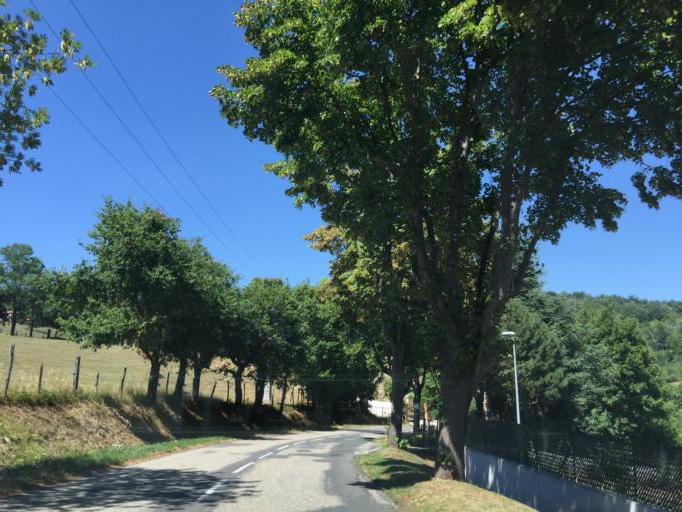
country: FR
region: Rhone-Alpes
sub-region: Departement de la Loire
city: Saint-Jean-Bonnefonds
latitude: 45.4562
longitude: 4.4495
